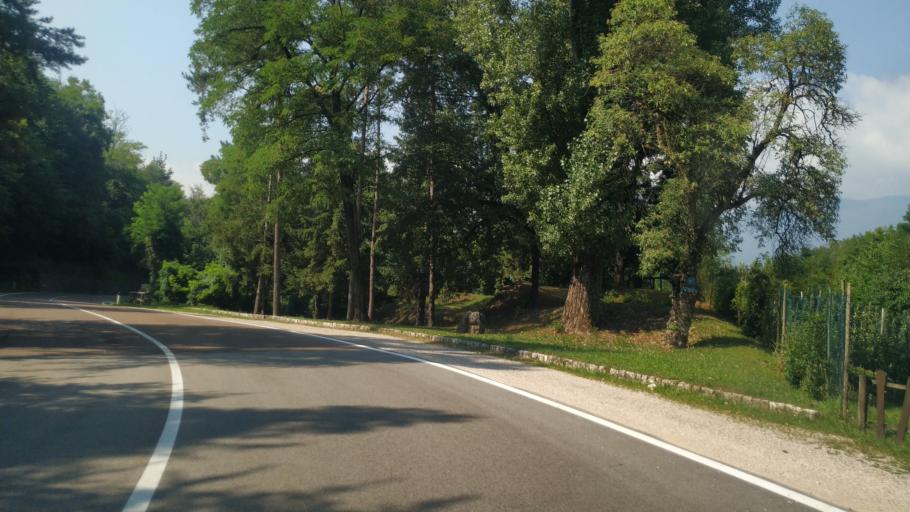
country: IT
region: Trentino-Alto Adige
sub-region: Provincia di Trento
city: Sanzeno
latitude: 46.3626
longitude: 11.0752
